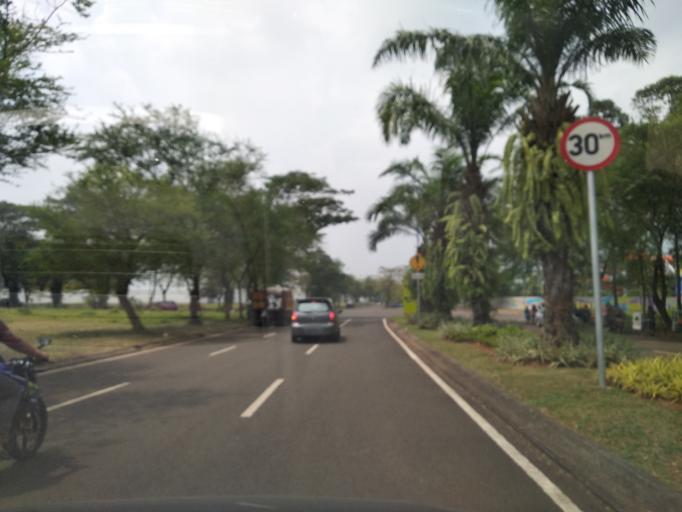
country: ID
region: West Java
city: Bekasi
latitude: -6.2955
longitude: 107.0500
